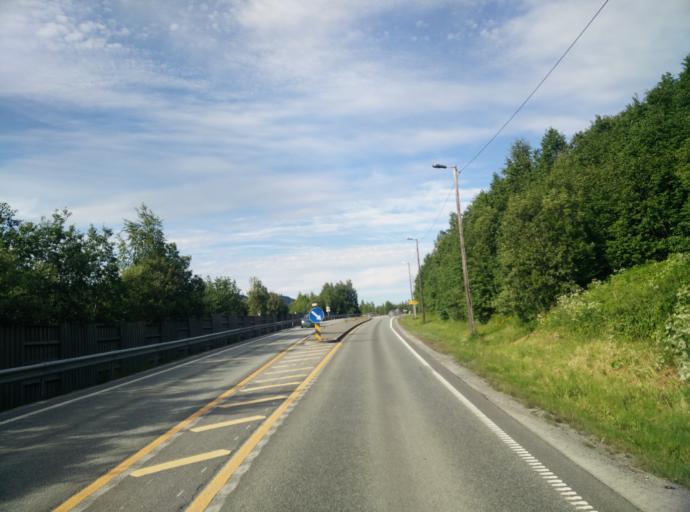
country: NO
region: Sor-Trondelag
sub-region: Orkdal
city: Orkanger
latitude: 63.3061
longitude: 9.8543
